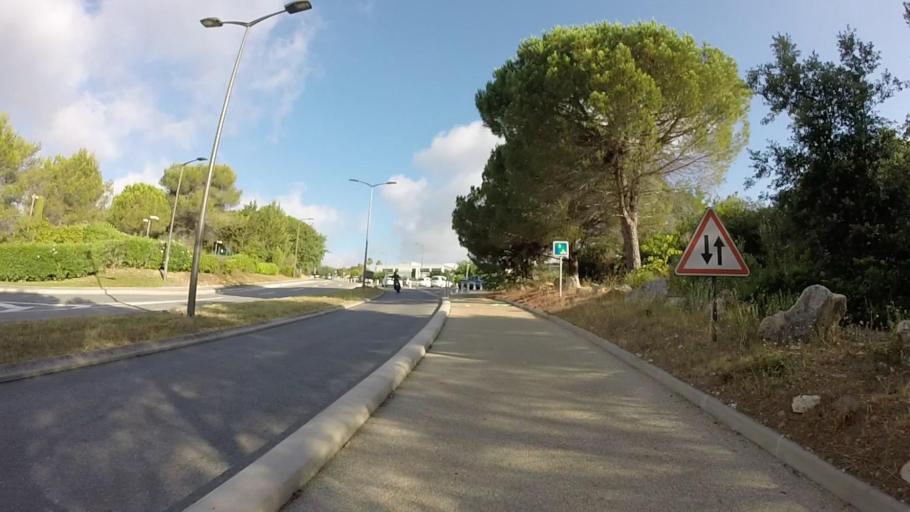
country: FR
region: Provence-Alpes-Cote d'Azur
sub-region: Departement des Alpes-Maritimes
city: Biot
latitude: 43.6230
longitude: 7.0621
